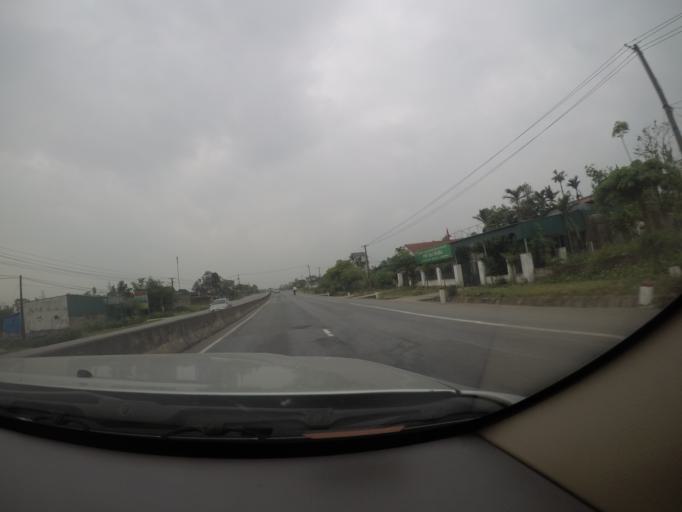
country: VN
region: Ha Tinh
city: Ky Anh
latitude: 18.1252
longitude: 106.2591
